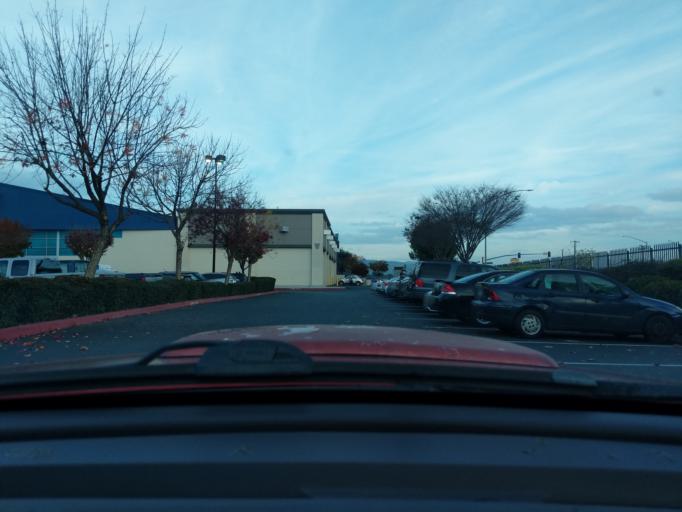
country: US
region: California
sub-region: Santa Clara County
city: Gilroy
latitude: 37.0045
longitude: -121.5527
